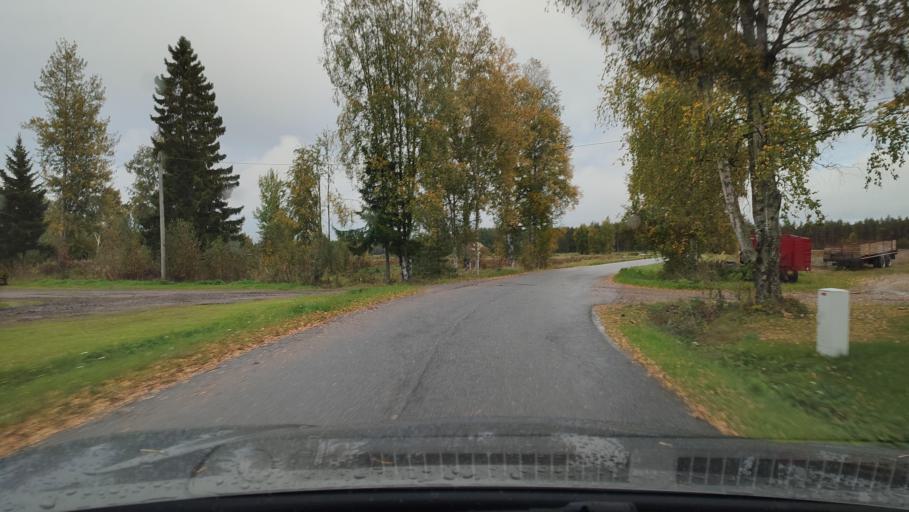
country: FI
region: Southern Ostrobothnia
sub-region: Suupohja
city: Karijoki
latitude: 62.2254
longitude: 21.6326
